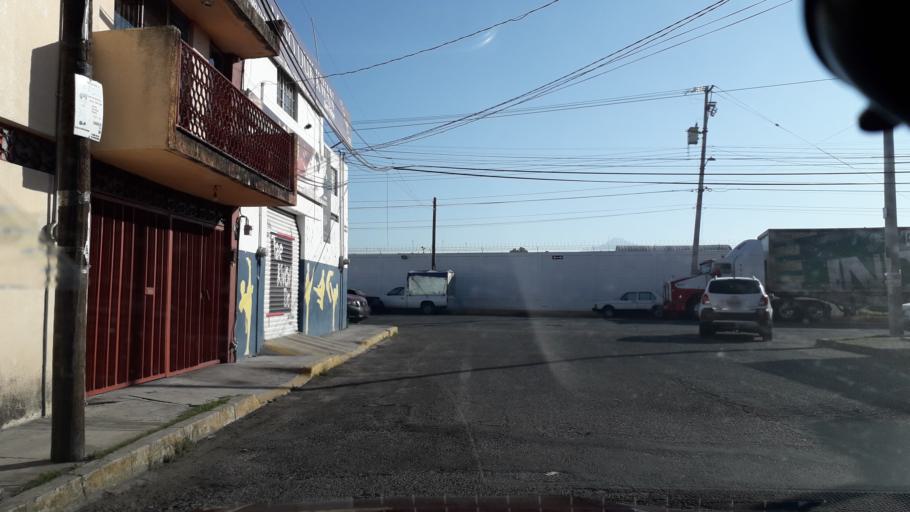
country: MX
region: Puebla
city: Puebla
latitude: 19.0632
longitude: -98.2177
